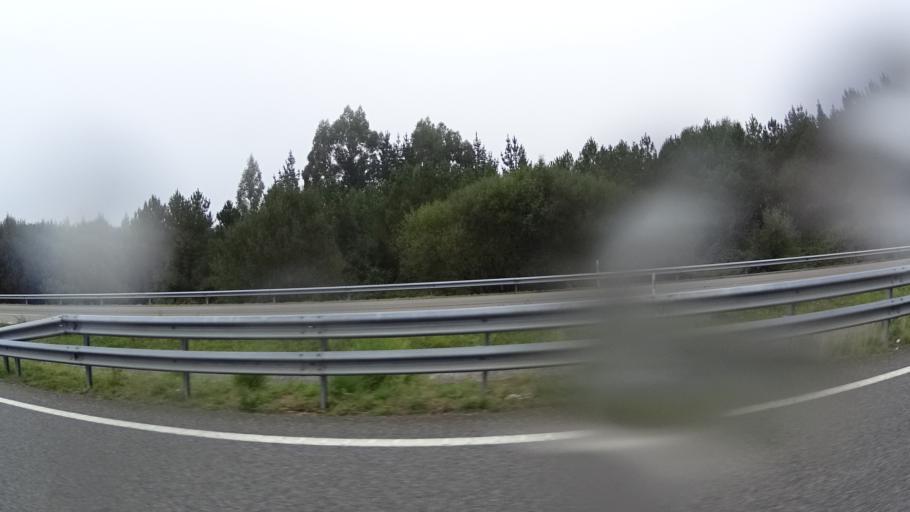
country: ES
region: Galicia
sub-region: Provincia de Lugo
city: Guitiriz
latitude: 43.1884
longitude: -7.9139
